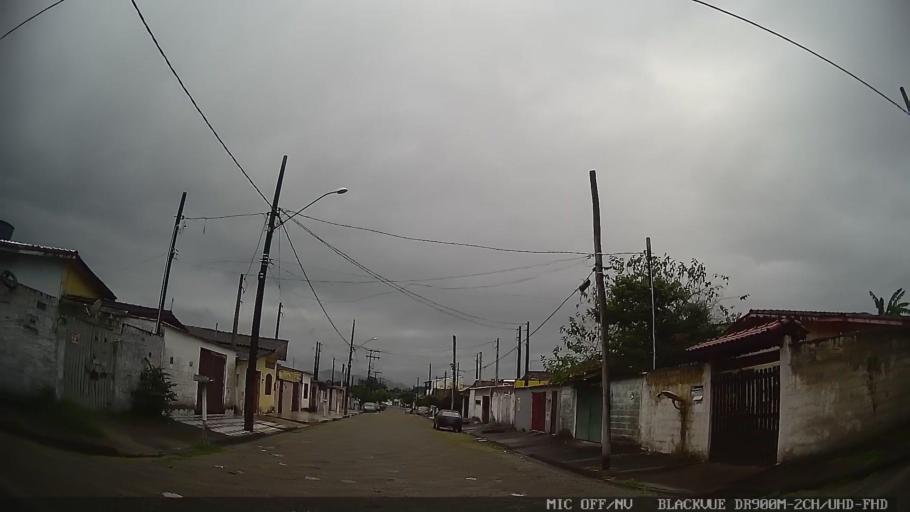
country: BR
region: Sao Paulo
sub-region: Itanhaem
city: Itanhaem
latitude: -24.1803
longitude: -46.8172
